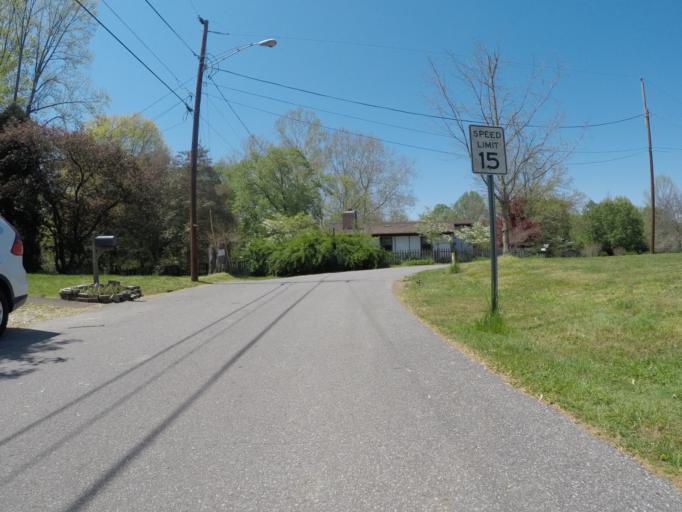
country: US
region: West Virginia
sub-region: Cabell County
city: Barboursville
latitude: 38.4085
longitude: -82.3014
